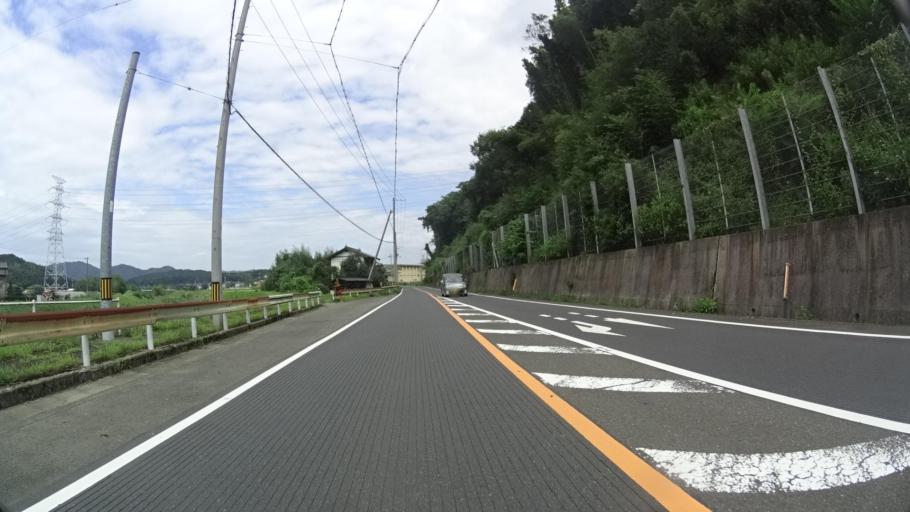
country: JP
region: Kyoto
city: Ayabe
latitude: 35.3430
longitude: 135.2170
